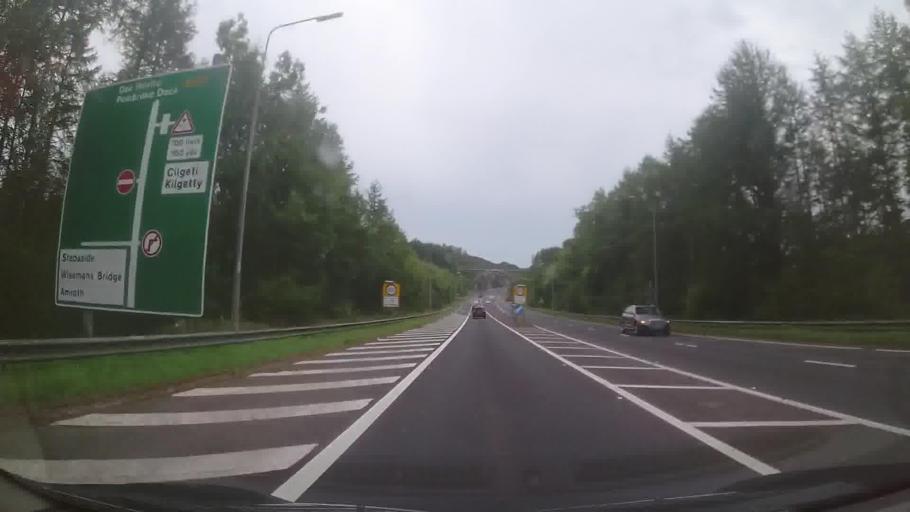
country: GB
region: Wales
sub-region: Pembrokeshire
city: Kilgetty
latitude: 51.7372
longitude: -4.7038
